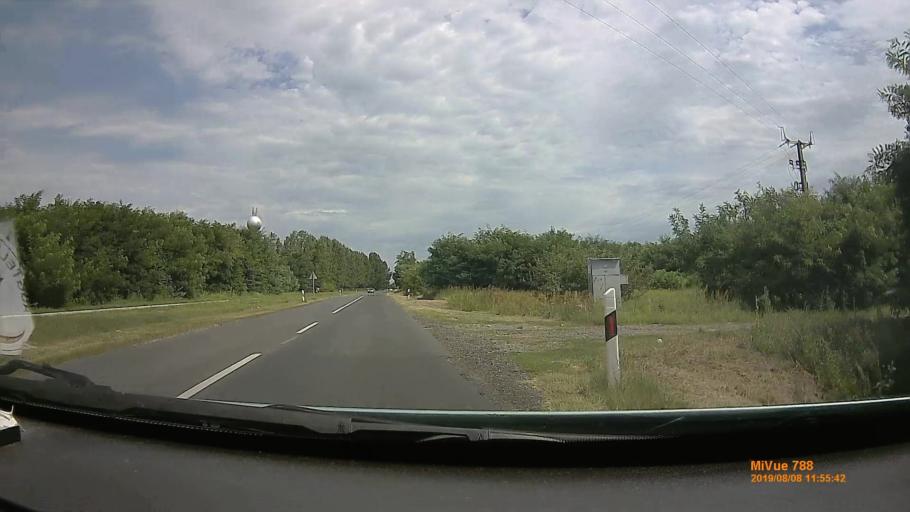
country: HU
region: Szabolcs-Szatmar-Bereg
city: Nyirmihalydi
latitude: 47.7441
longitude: 21.9830
